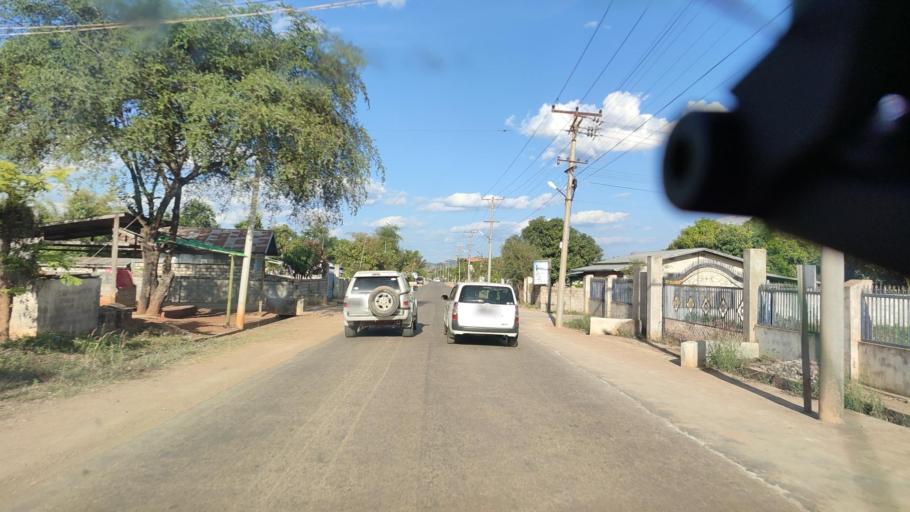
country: MM
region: Shan
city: Taunggyi
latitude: 20.7596
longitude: 97.6665
